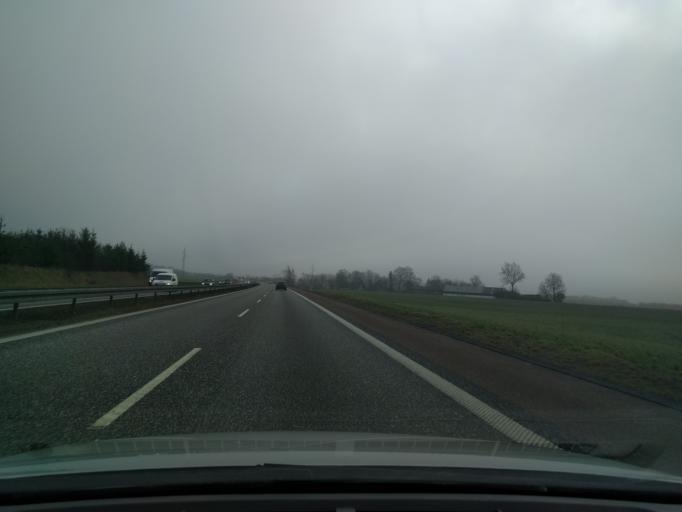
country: DK
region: Zealand
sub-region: Ringsted Kommune
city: Ringsted
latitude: 55.4473
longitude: 11.6829
